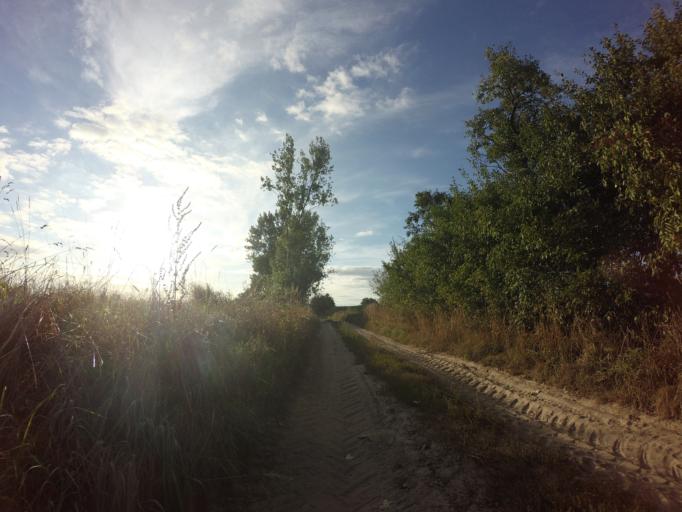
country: PL
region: West Pomeranian Voivodeship
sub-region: Powiat choszczenski
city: Krzecin
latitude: 53.1115
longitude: 15.4407
